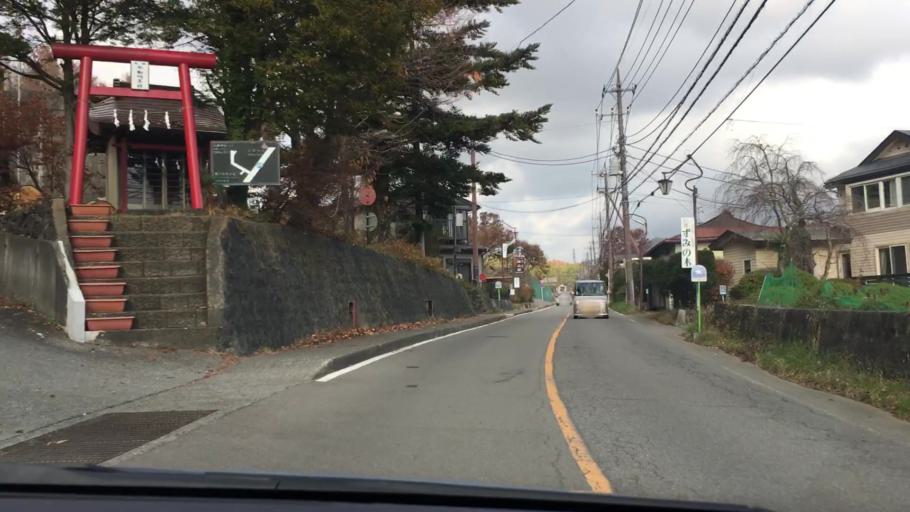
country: JP
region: Shizuoka
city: Gotemba
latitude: 35.4304
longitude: 138.9047
